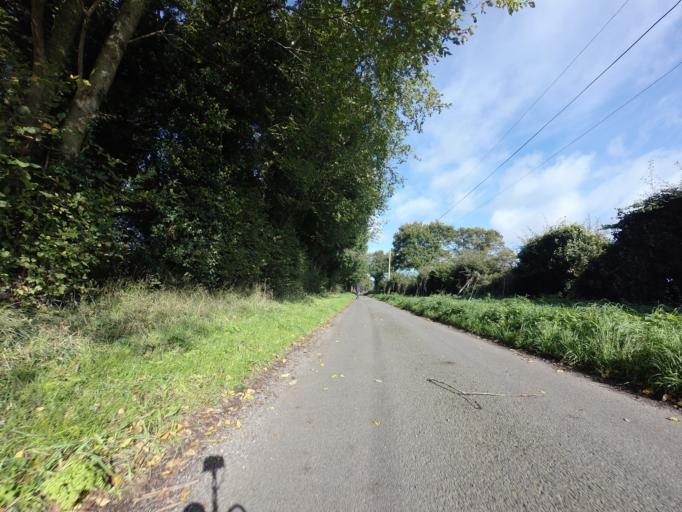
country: GB
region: England
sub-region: Norfolk
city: Fakenham
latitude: 52.8854
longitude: 0.6840
